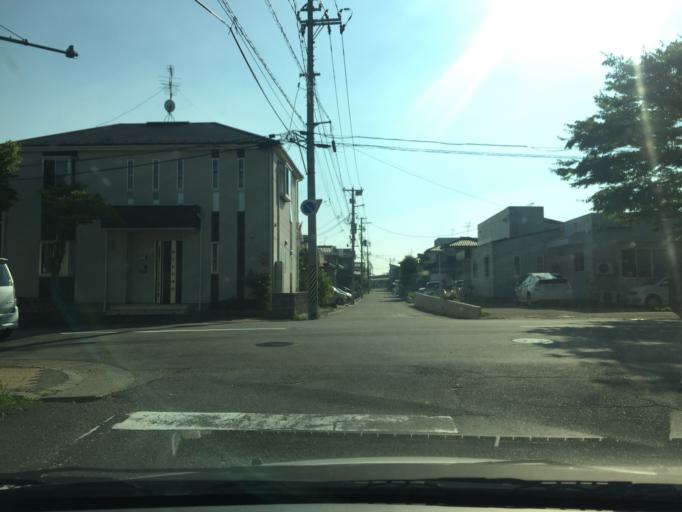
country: JP
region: Niigata
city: Niigata-shi
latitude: 37.8916
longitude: 139.0466
